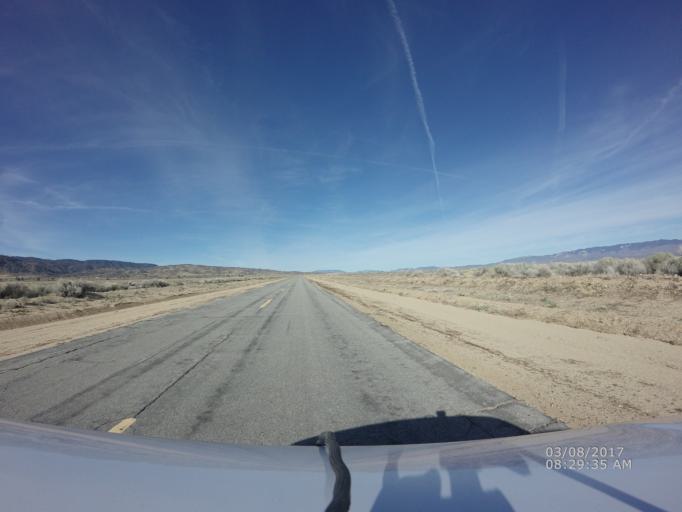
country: US
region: California
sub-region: Los Angeles County
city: Green Valley
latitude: 34.7461
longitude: -118.4756
